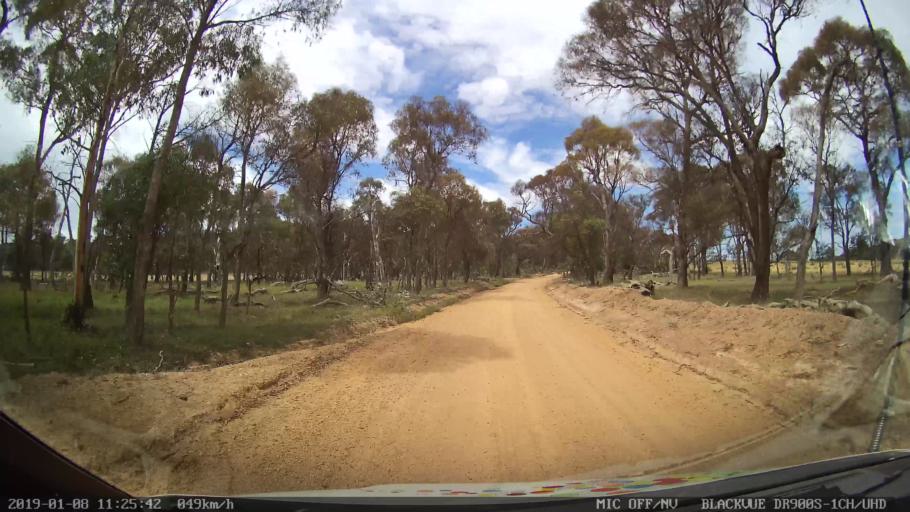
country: AU
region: New South Wales
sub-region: Guyra
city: Guyra
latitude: -30.2754
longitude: 151.5611
